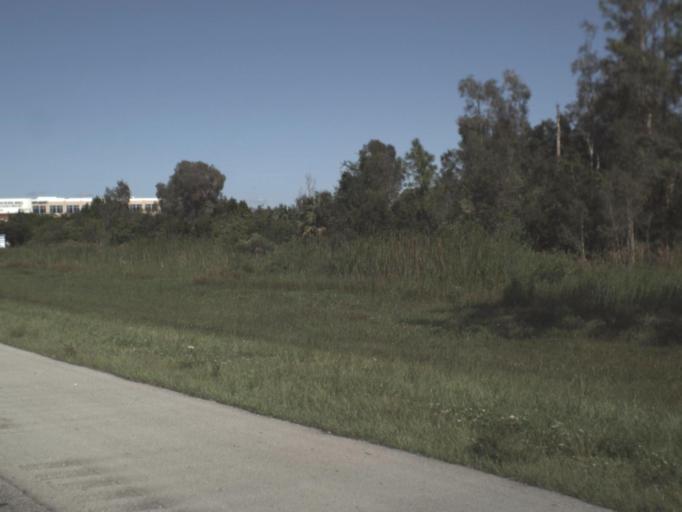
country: US
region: Florida
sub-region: Lee County
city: Fort Myers
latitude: 26.6237
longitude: -81.8055
